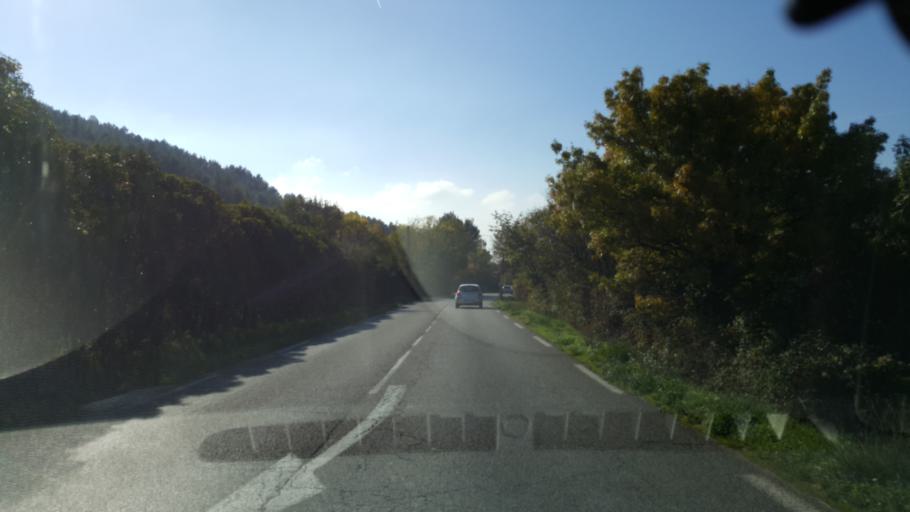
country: FR
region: Provence-Alpes-Cote d'Azur
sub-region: Departement du Var
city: Saint-Zacharie
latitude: 43.3758
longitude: 5.6757
